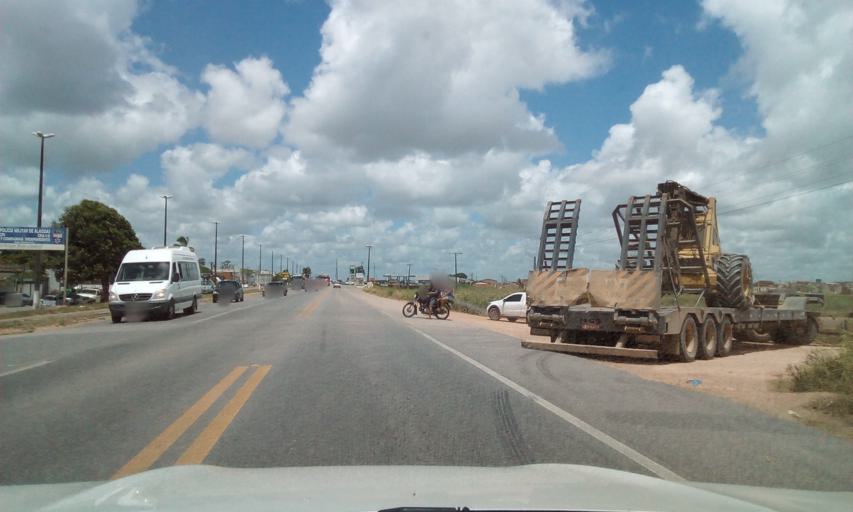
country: BR
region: Alagoas
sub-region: Sao Miguel Dos Campos
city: Sao Miguel dos Campos
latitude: -9.8037
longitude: -36.1134
